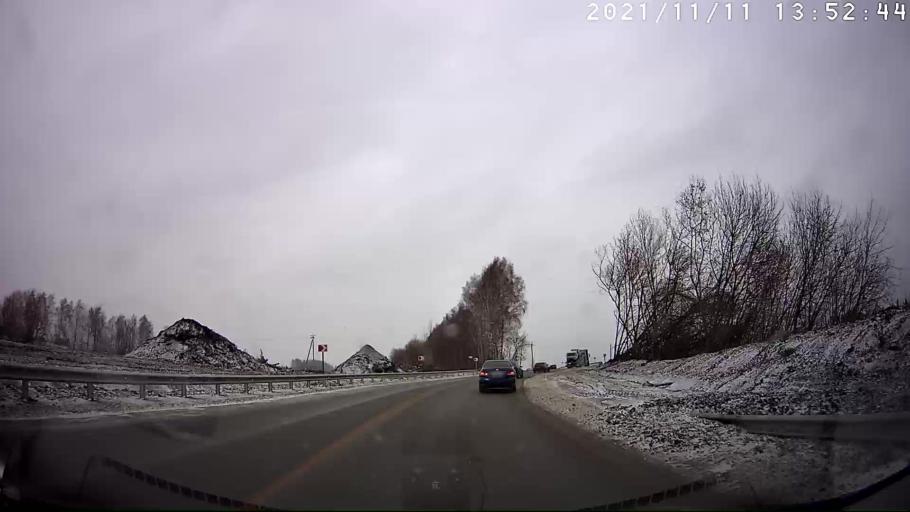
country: RU
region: Chuvashia
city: Shikhazany
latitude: 55.5724
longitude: 47.4105
